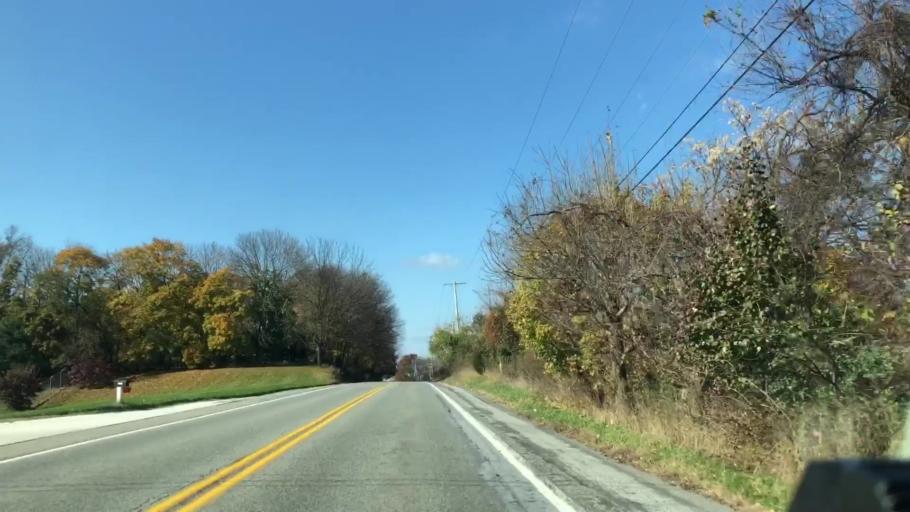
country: US
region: Pennsylvania
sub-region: Chester County
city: Kenilworth
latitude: 40.2184
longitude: -75.6084
